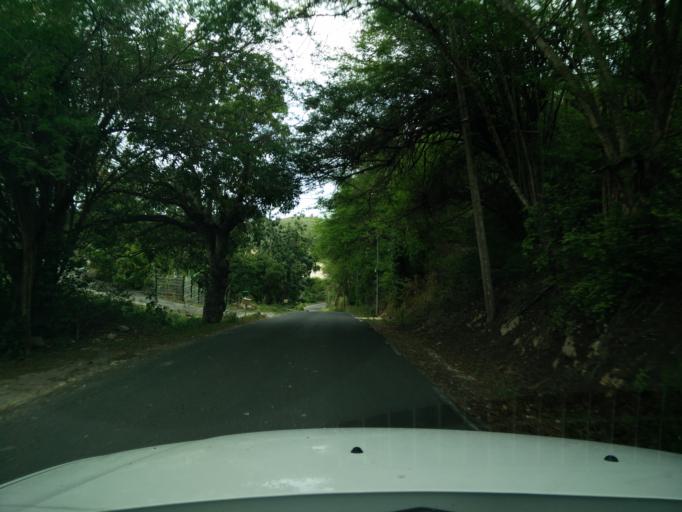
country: GP
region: Guadeloupe
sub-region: Guadeloupe
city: Le Gosier
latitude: 16.2318
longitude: -61.4421
